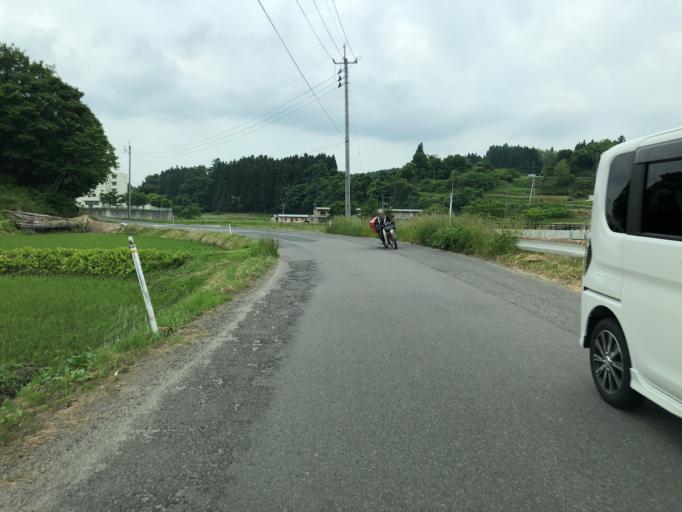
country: JP
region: Fukushima
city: Funehikimachi-funehiki
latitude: 37.4363
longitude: 140.6487
